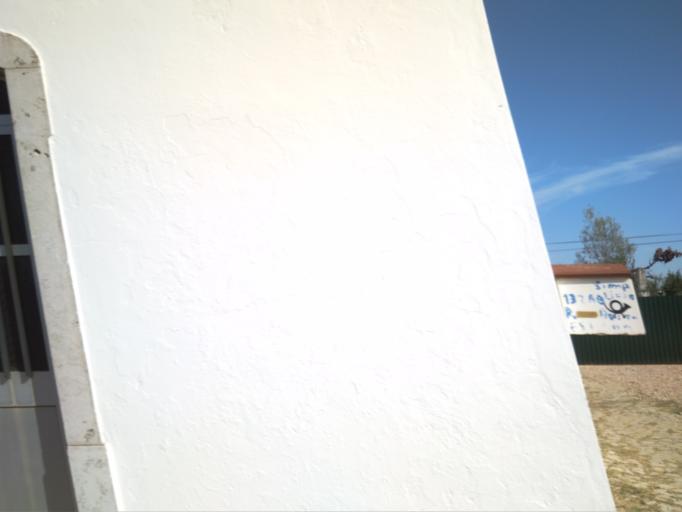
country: PT
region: Faro
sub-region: Faro
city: Santa Barbara de Nexe
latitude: 37.0679
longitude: -7.9563
